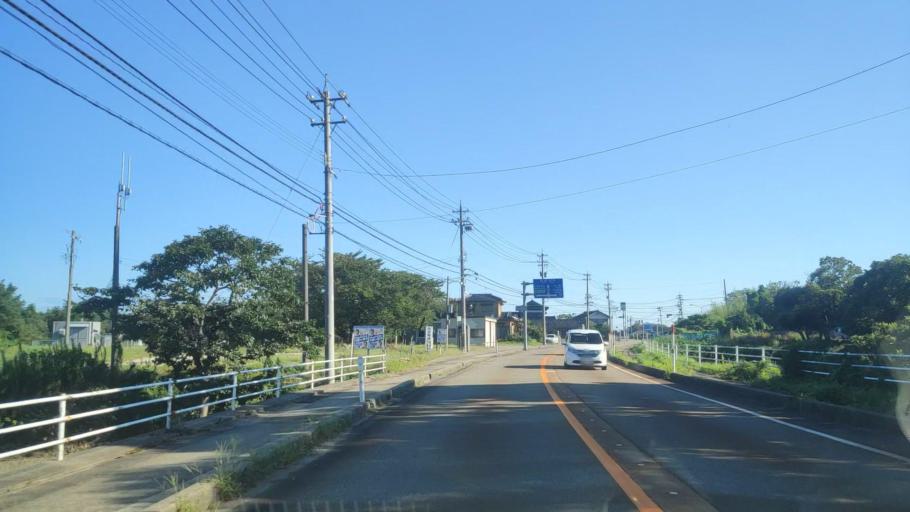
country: JP
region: Ishikawa
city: Hakui
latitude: 36.8425
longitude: 136.7650
